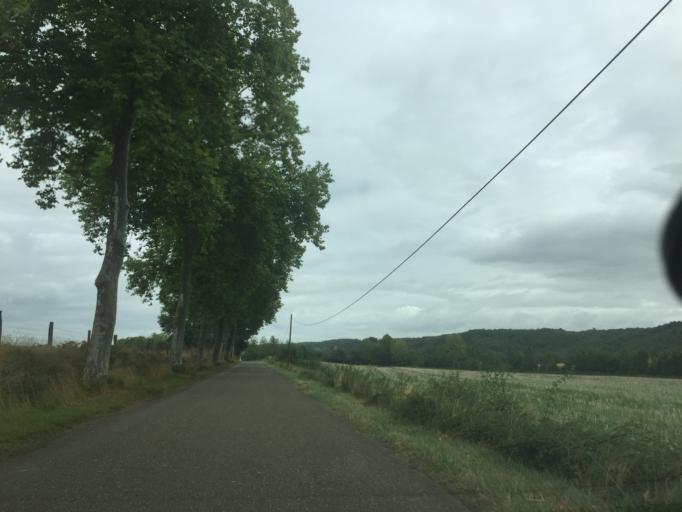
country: FR
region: Midi-Pyrenees
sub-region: Departement du Gers
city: Mielan
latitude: 43.5180
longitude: 0.3255
